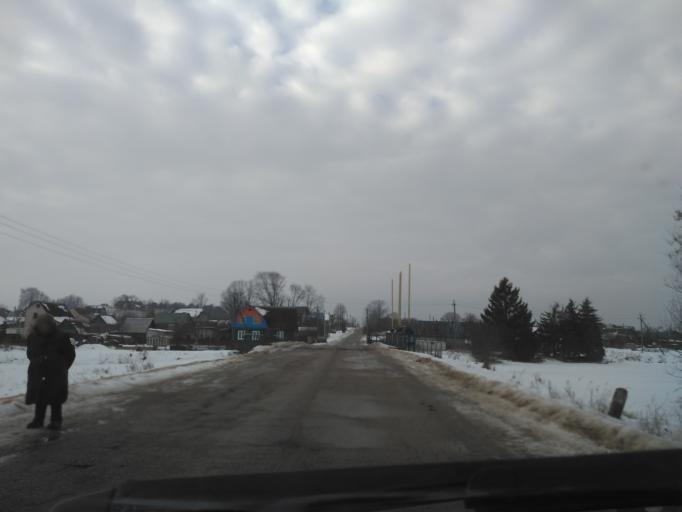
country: BY
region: Minsk
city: Zamostochcha
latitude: 53.8905
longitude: 27.9133
